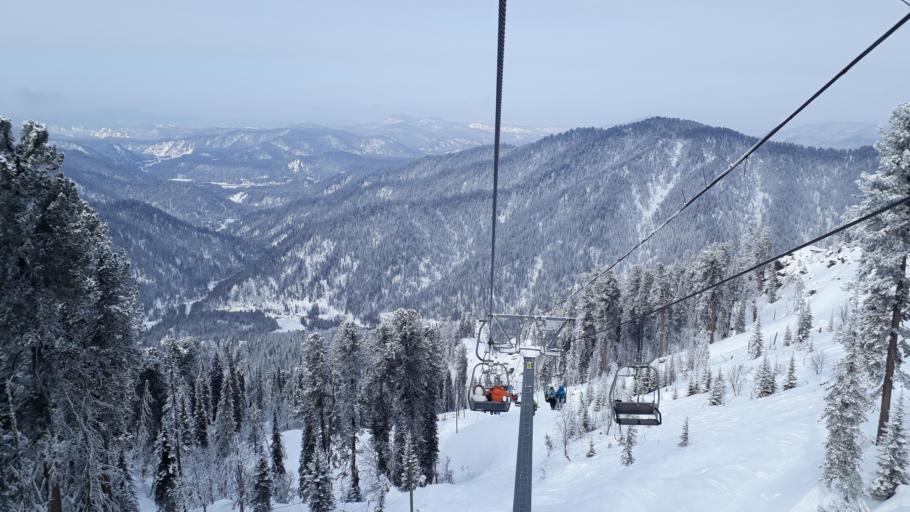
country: RU
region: Altay
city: Iogach
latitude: 51.7321
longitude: 87.2997
